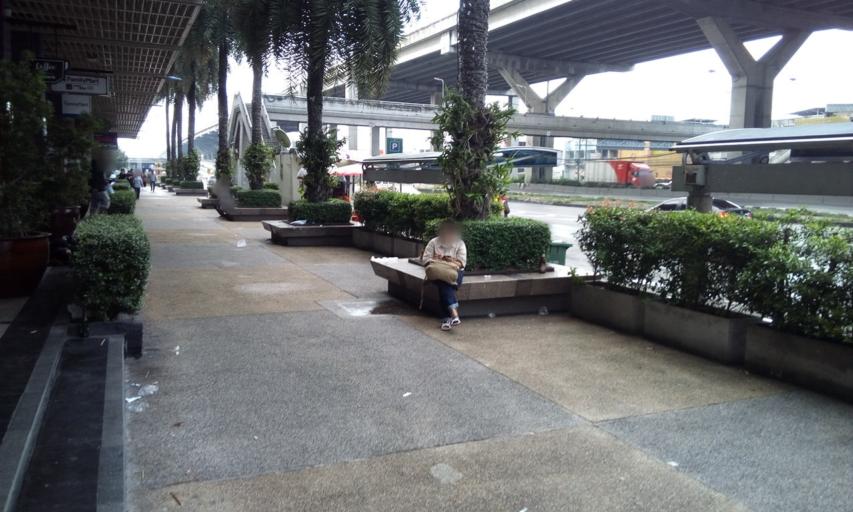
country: TH
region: Phra Nakhon Si Ayutthaya
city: Ban Bang Kadi Pathum Thani
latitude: 13.9871
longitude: 100.6165
